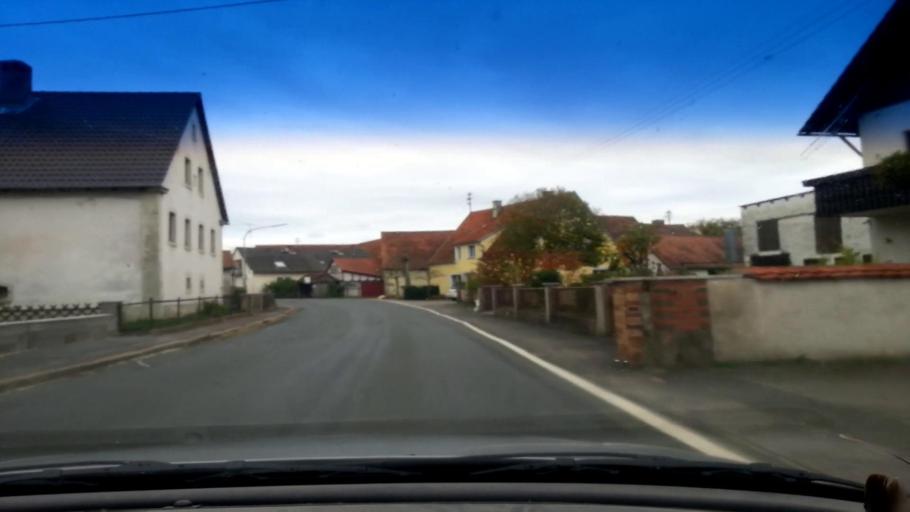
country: DE
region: Bavaria
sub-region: Upper Franconia
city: Burgwindheim
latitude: 49.8704
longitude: 10.6360
